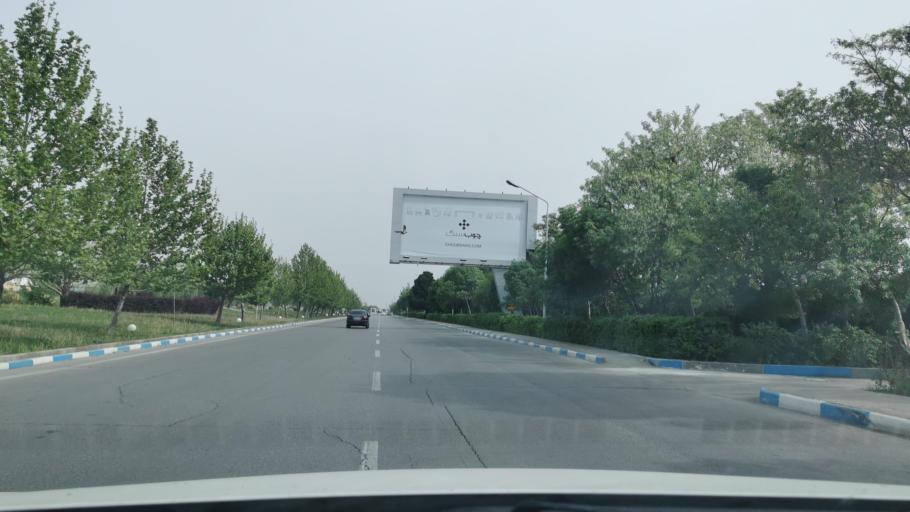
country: IR
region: Razavi Khorasan
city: Mashhad
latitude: 36.2319
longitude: 59.6346
